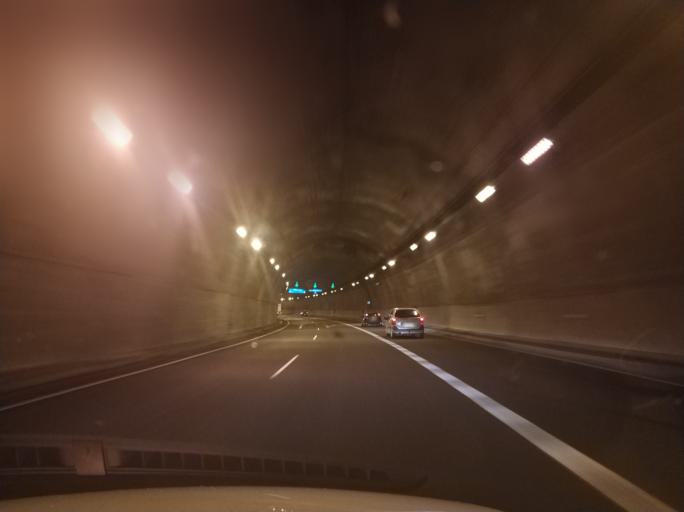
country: ES
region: Cantabria
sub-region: Provincia de Cantabria
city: Torrelavega
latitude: 43.3574
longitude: -4.0387
